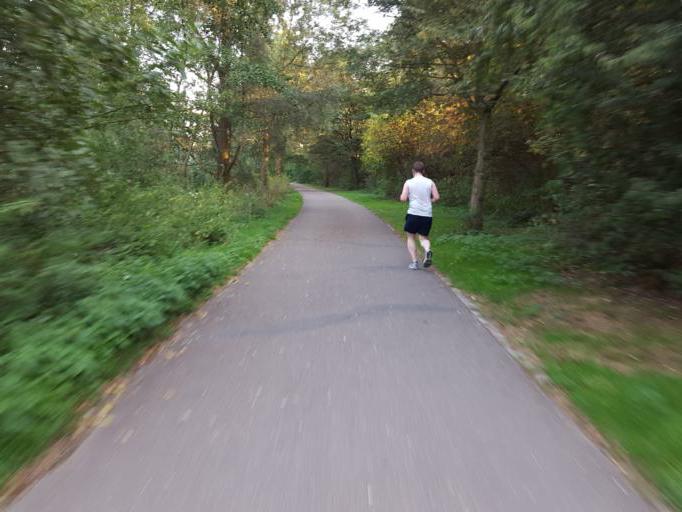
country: DE
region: Baden-Wuerttemberg
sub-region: Karlsruhe Region
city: Karlsruhe
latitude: 48.9970
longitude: 8.3735
